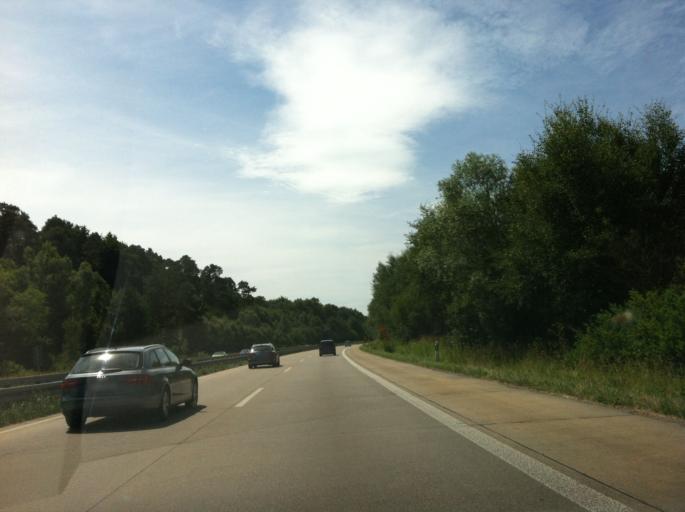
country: DE
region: Hesse
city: Dieburg
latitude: 49.8978
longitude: 8.8664
